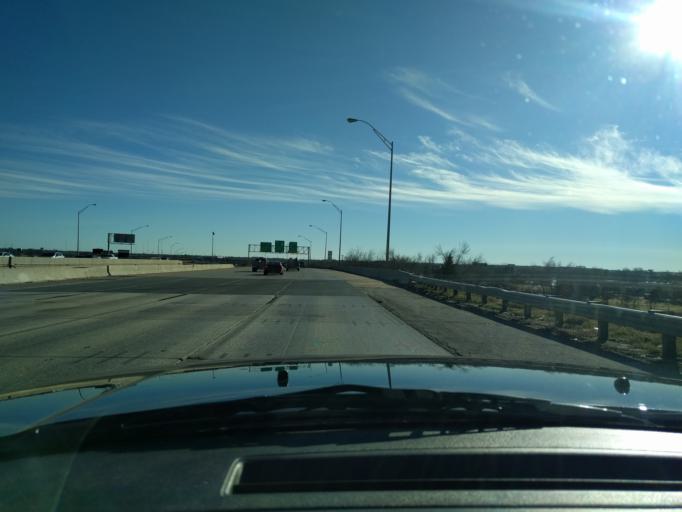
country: US
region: Oklahoma
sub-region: Oklahoma County
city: Oklahoma City
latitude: 35.4715
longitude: -97.5796
